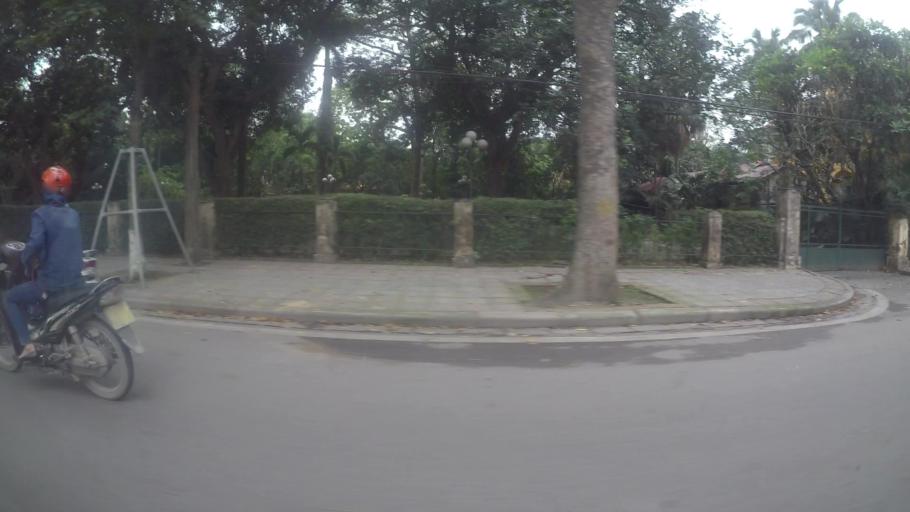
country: VN
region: Ha Noi
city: Hanoi
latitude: 21.0349
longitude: 105.8391
